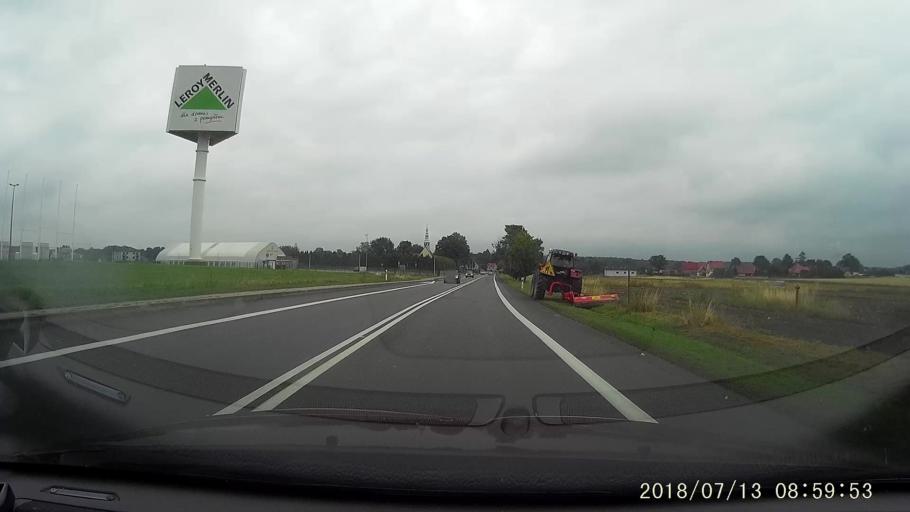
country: PL
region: Lower Silesian Voivodeship
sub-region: Powiat zgorzelecki
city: Lagow
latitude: 51.1565
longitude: 15.0369
